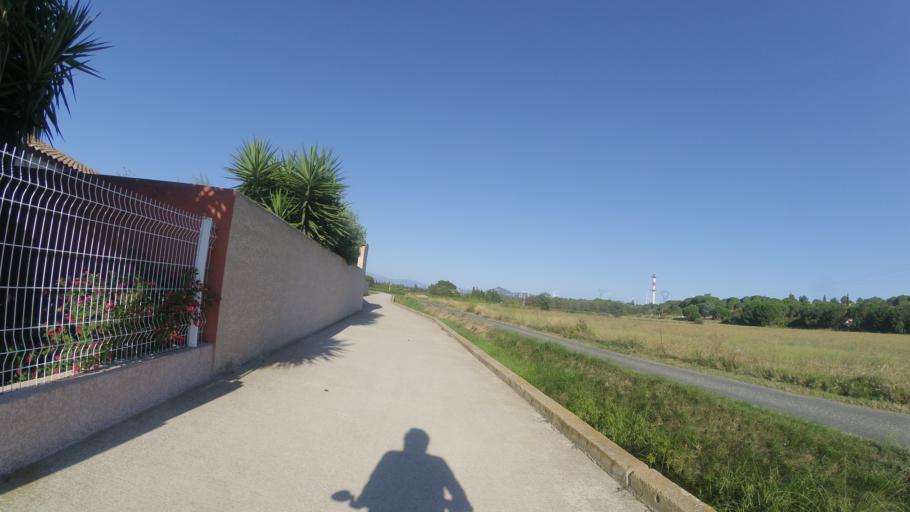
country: FR
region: Languedoc-Roussillon
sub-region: Departement des Pyrenees-Orientales
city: Baho
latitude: 42.7063
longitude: 2.8212
